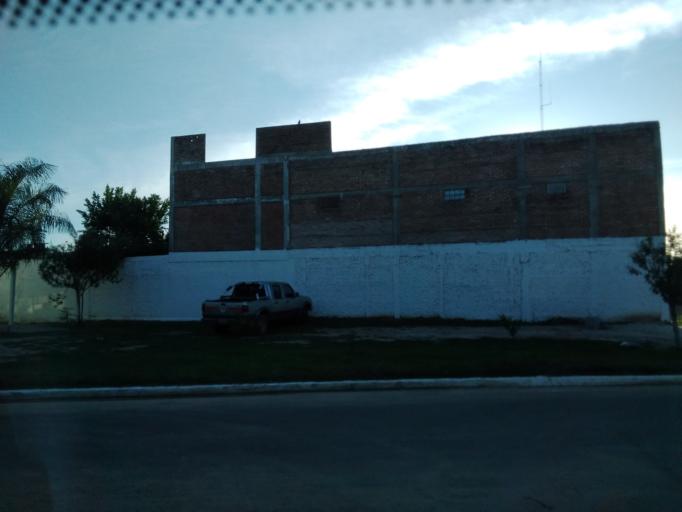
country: AR
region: Corrientes
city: Corrientes
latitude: -27.4623
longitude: -58.7860
